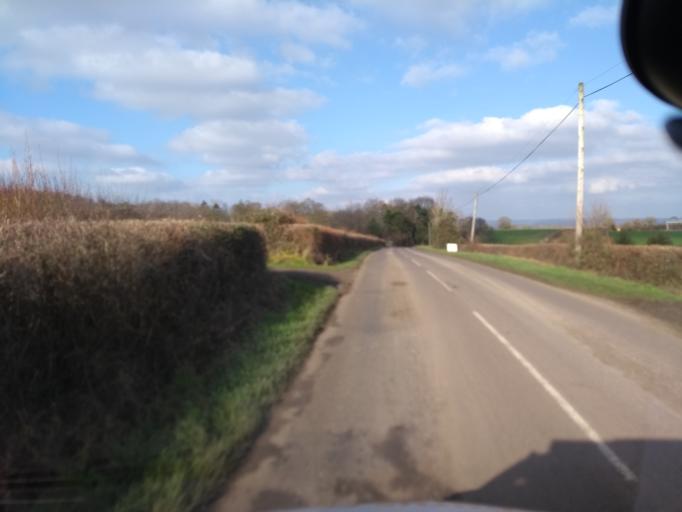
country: GB
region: England
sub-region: Somerset
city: Creech Saint Michael
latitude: 50.9651
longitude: -3.0526
